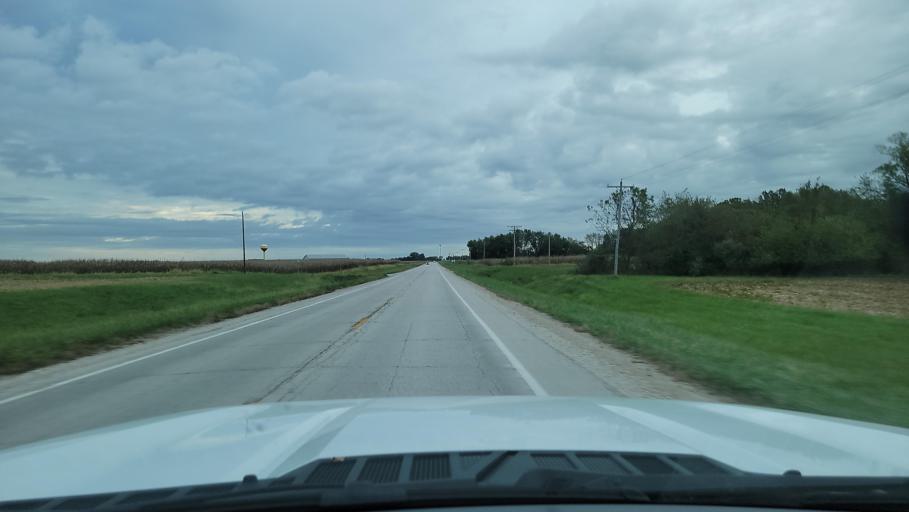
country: US
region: Illinois
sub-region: Schuyler County
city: Rushville
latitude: 40.1085
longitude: -90.5908
